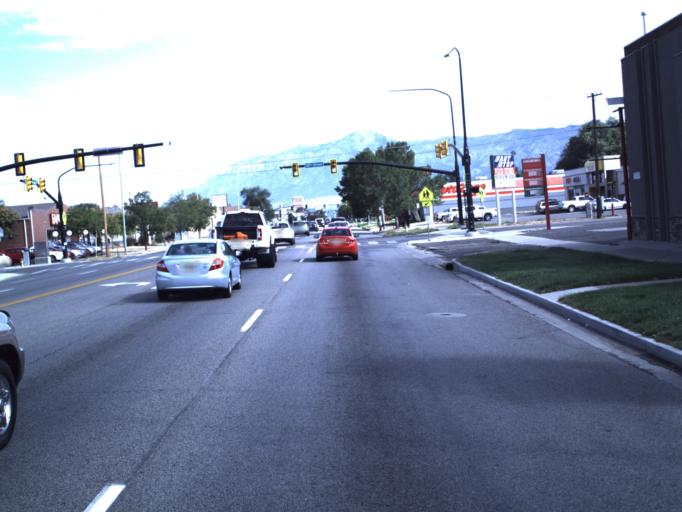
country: US
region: Utah
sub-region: Weber County
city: South Ogden
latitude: 41.2055
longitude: -111.9707
